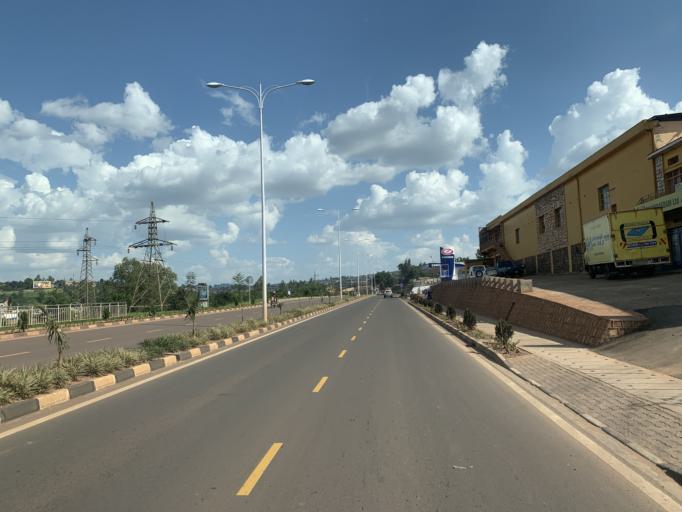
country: RW
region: Kigali
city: Kigali
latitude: -1.9669
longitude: 30.0822
